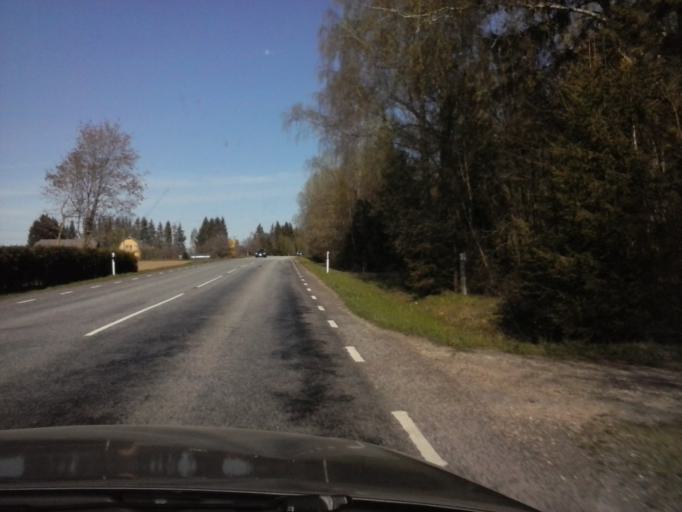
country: EE
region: Tartu
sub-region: Elva linn
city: Elva
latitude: 58.1445
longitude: 26.2205
